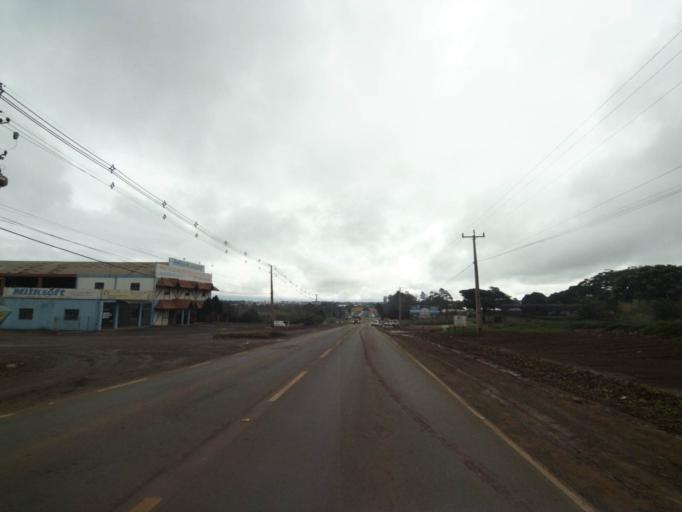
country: BR
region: Parana
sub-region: Marechal Candido Rondon
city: Marechal Candido Rondon
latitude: -24.5684
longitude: -54.0302
